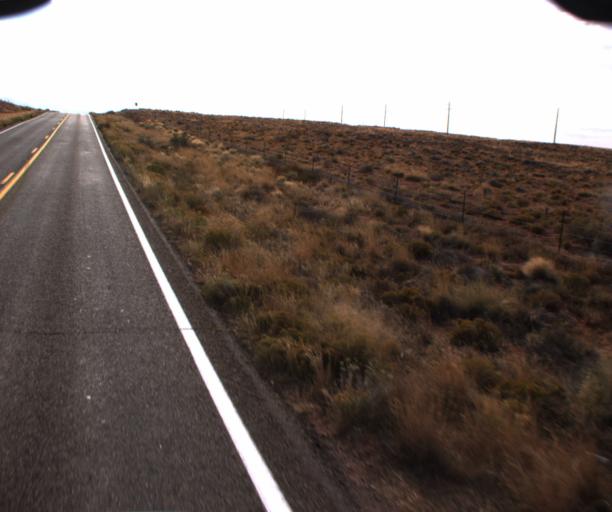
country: US
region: Arizona
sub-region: Apache County
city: Many Farms
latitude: 36.5345
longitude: -109.5132
